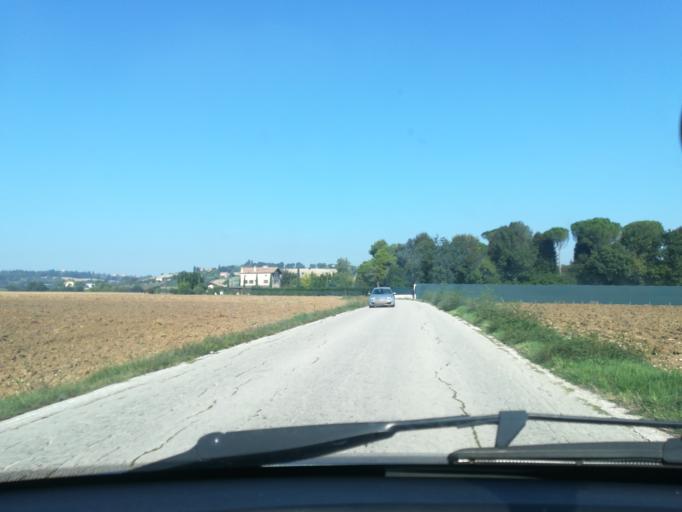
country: IT
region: The Marches
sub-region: Provincia di Macerata
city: Macerata
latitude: 43.2676
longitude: 13.4520
